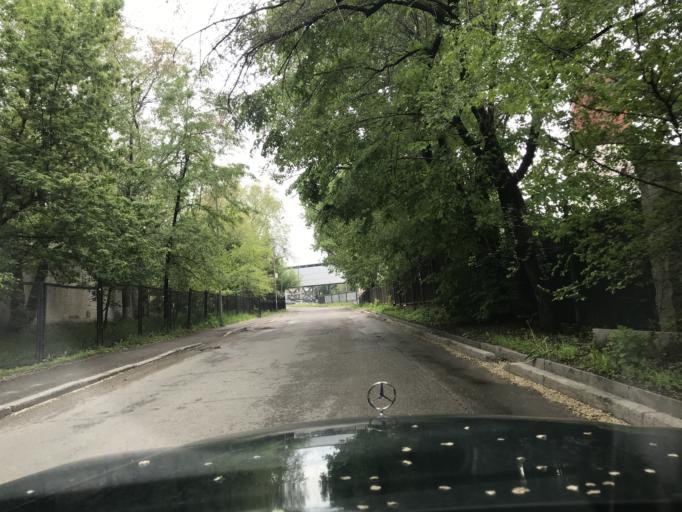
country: KZ
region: Almaty Qalasy
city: Almaty
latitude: 43.2058
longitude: 76.8709
